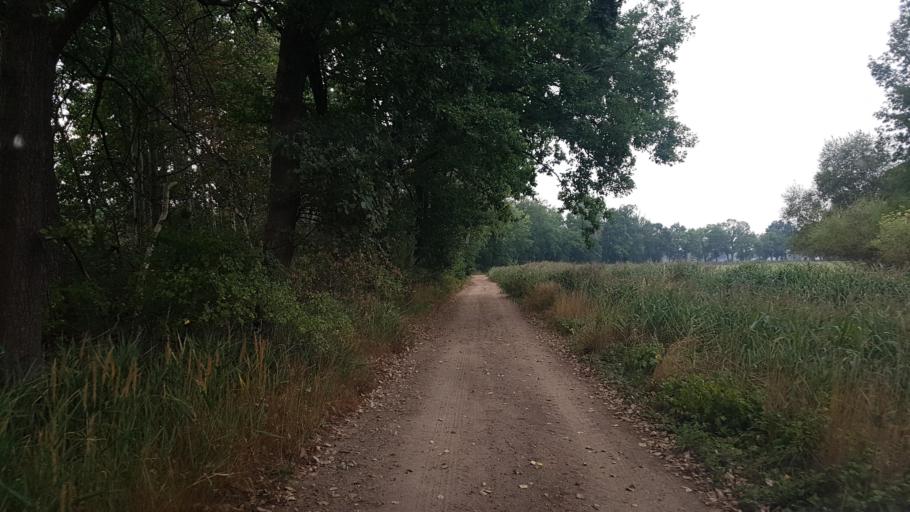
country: DE
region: Brandenburg
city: Bronkow
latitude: 51.6234
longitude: 13.9093
